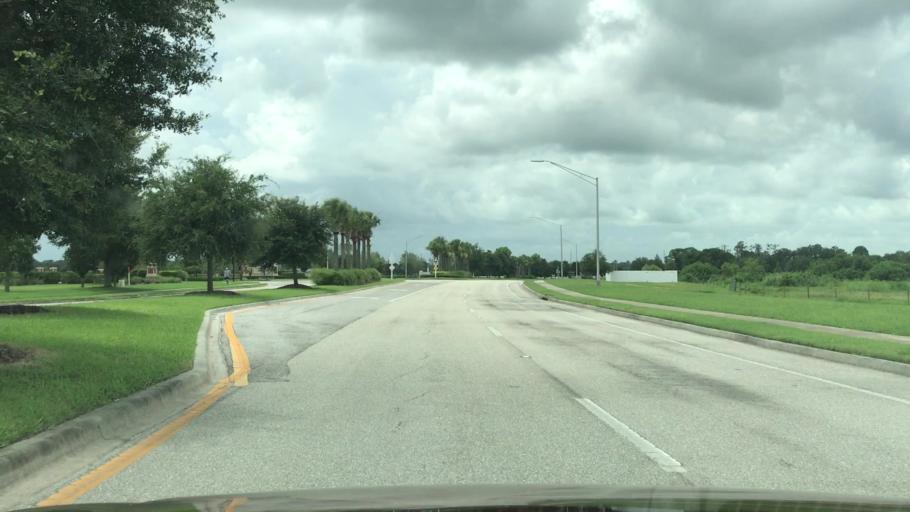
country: US
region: Florida
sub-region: Sarasota County
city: The Meadows
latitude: 27.4401
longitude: -82.4130
